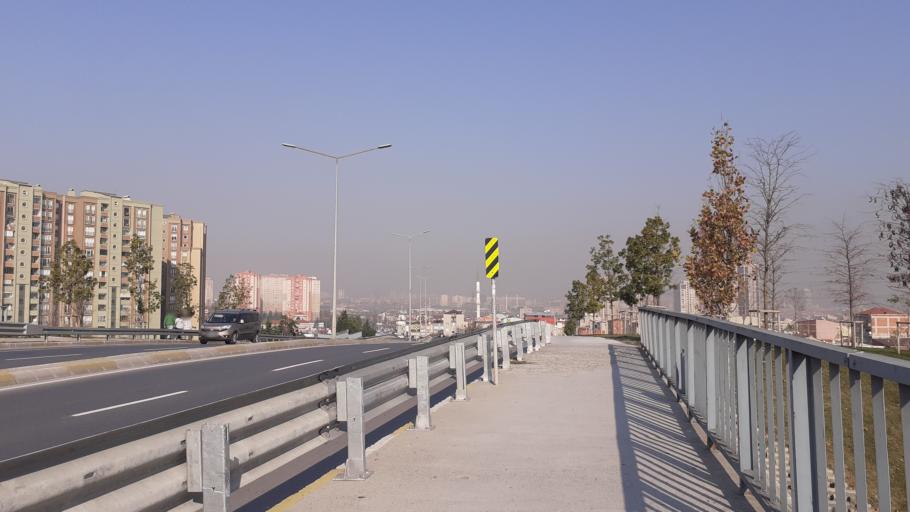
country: TR
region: Istanbul
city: Mahmutbey
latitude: 41.0494
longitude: 28.7940
